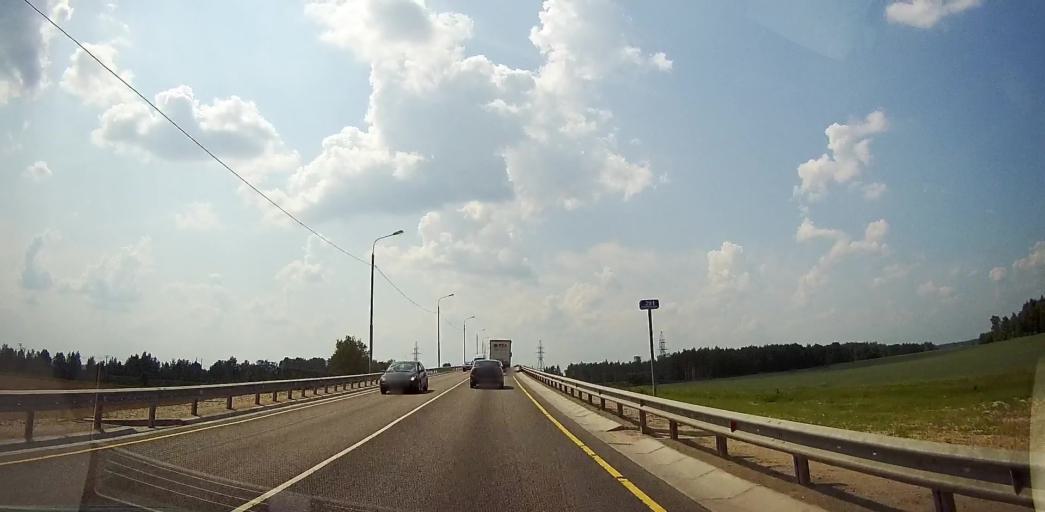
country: RU
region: Moskovskaya
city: Malino
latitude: 55.1186
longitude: 38.2080
